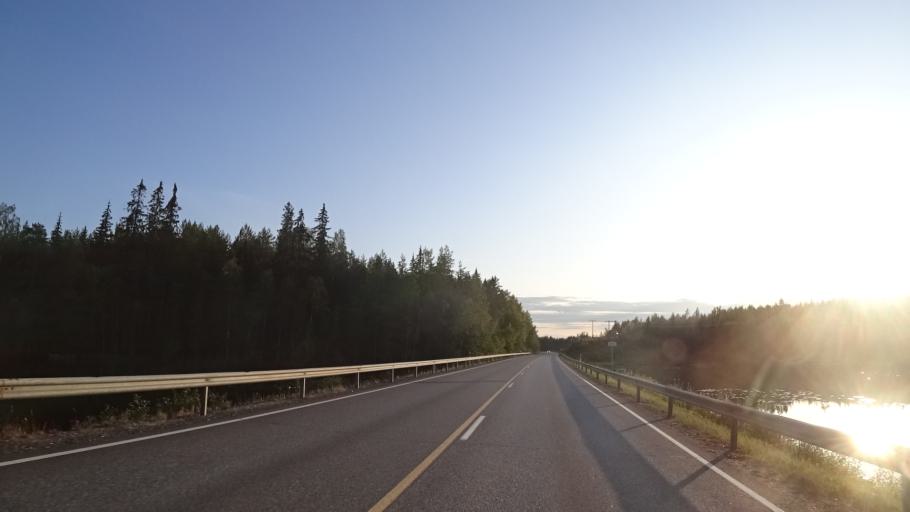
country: FI
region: South Karelia
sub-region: Lappeenranta
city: Ylaemaa
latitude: 60.8165
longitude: 28.0775
